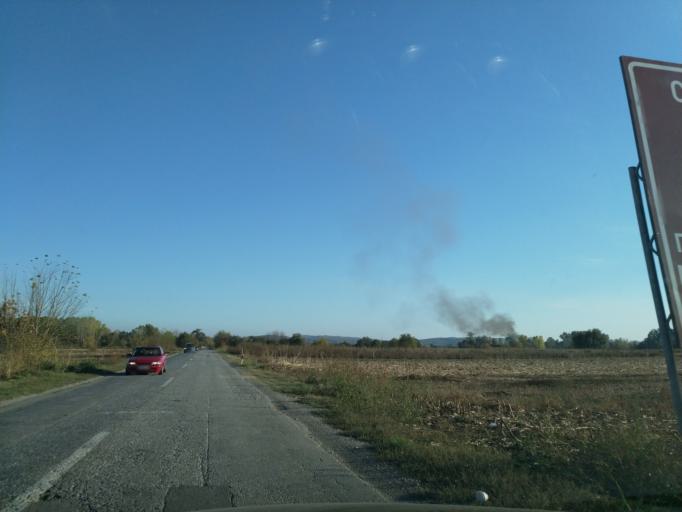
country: RS
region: Central Serbia
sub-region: Pomoravski Okrug
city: Svilajnac
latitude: 44.2330
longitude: 21.1403
